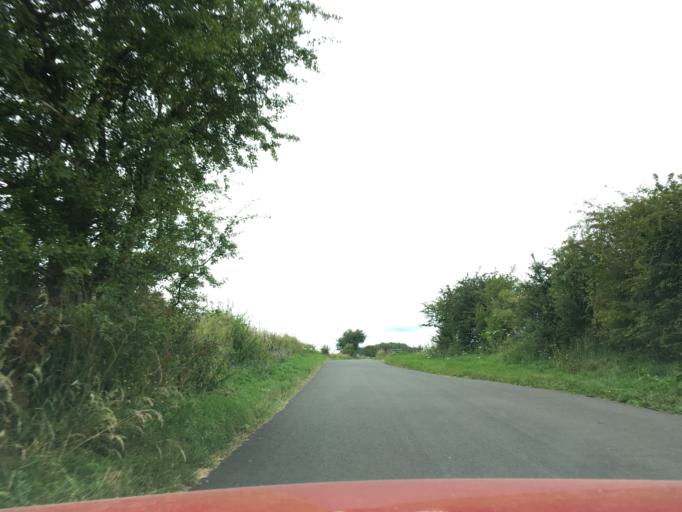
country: GB
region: England
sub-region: Gloucestershire
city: Shipton Village
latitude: 51.8961
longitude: -1.9152
